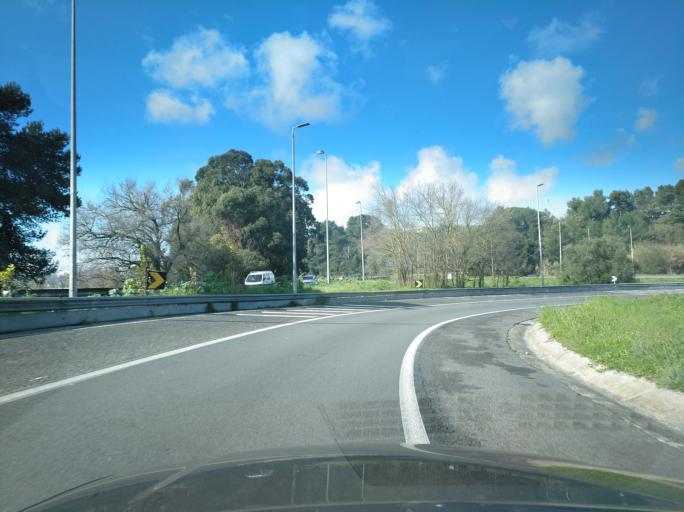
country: PT
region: Setubal
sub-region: Almada
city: Pragal
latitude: 38.6648
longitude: -9.1726
